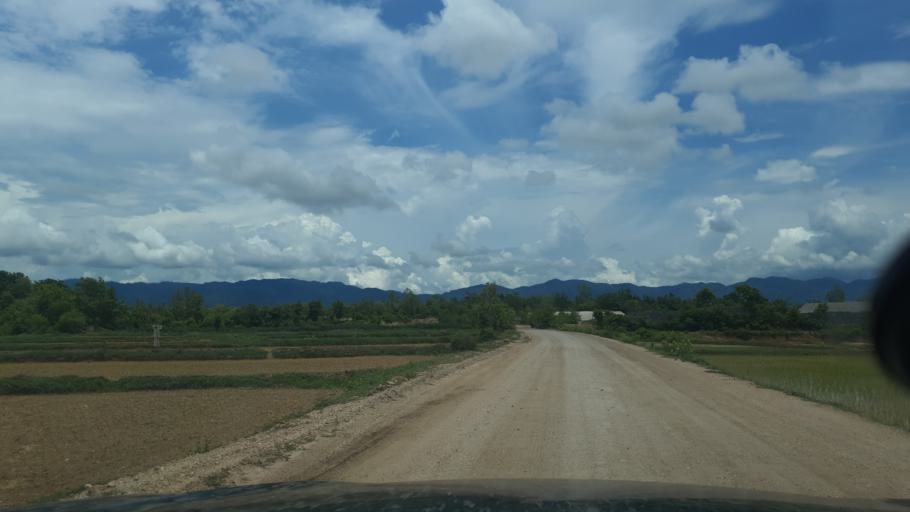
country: TH
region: Lampang
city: Sop Prap
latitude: 17.9365
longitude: 99.3628
